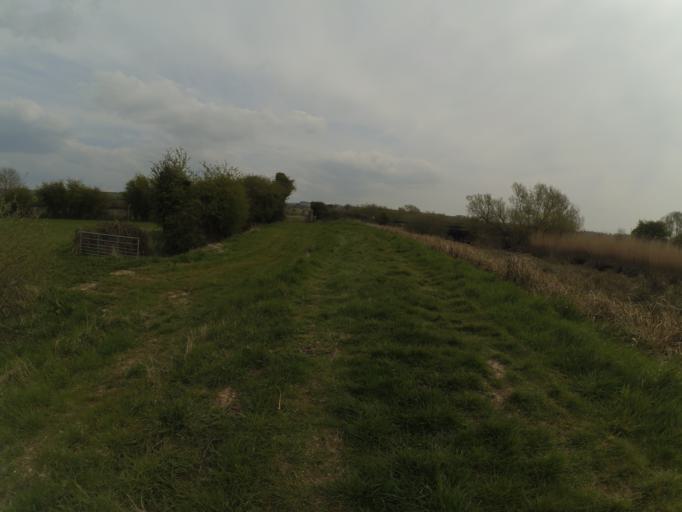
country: GB
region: England
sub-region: West Sussex
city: Arundel
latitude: 50.8740
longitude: -0.5365
